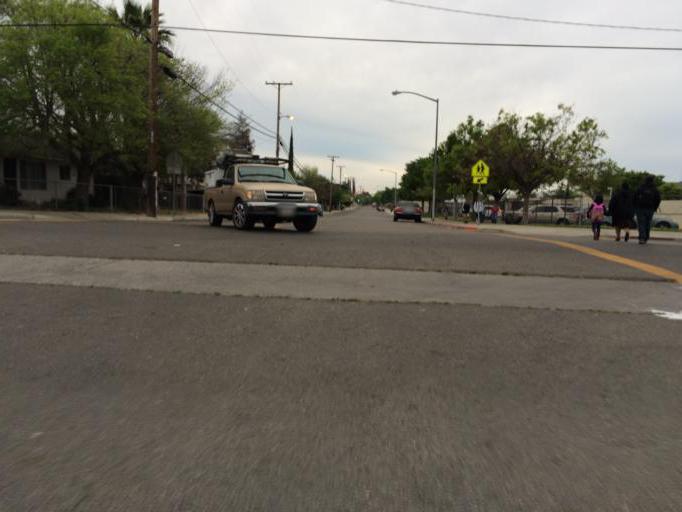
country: US
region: California
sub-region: Fresno County
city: Fresno
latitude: 36.7534
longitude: -119.7499
